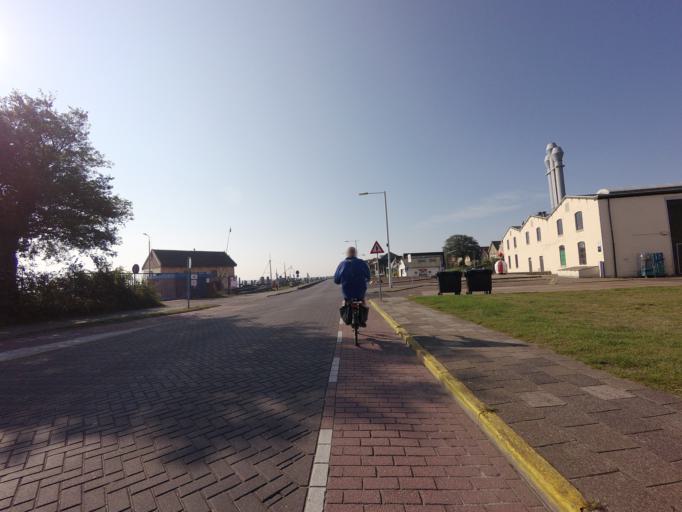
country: NL
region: Friesland
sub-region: Gemeente Terschelling
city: West-Terschelling
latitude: 53.3624
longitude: 5.2177
